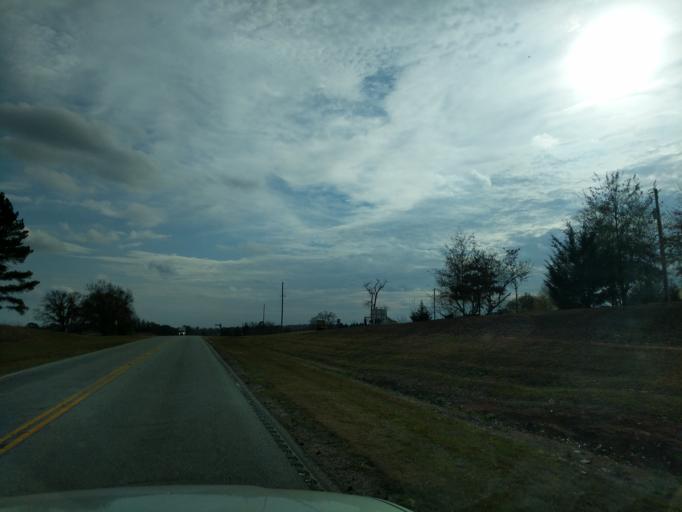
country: US
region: Georgia
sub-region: Franklin County
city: Gumlog
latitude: 34.5769
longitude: -83.0502
